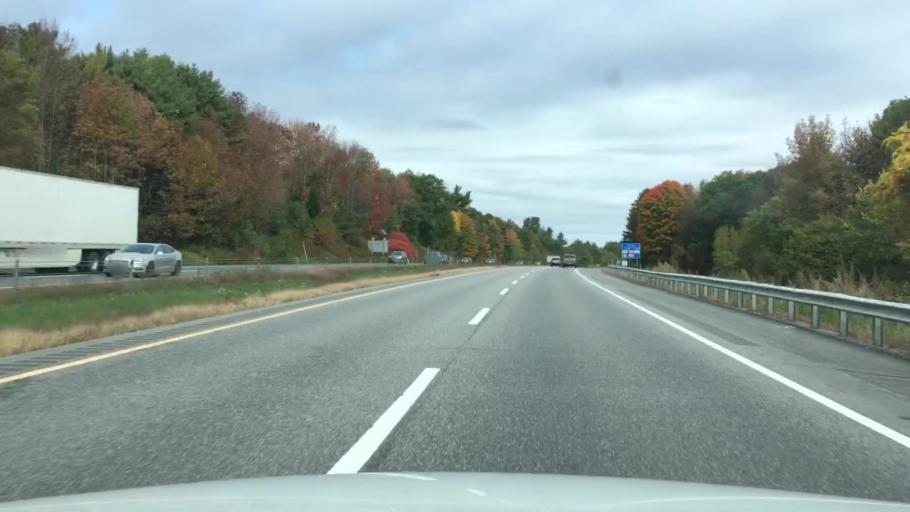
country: US
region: Maine
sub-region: Kennebec County
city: Augusta
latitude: 44.3279
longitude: -69.8148
